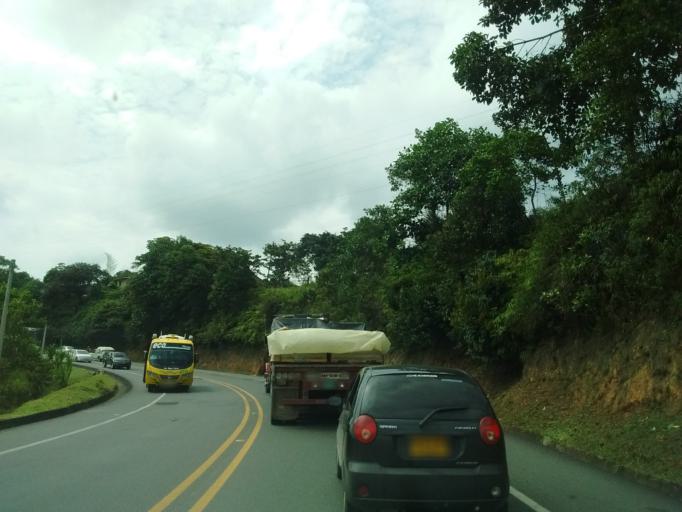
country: CO
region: Cauca
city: Caldono
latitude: 2.7896
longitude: -76.5518
